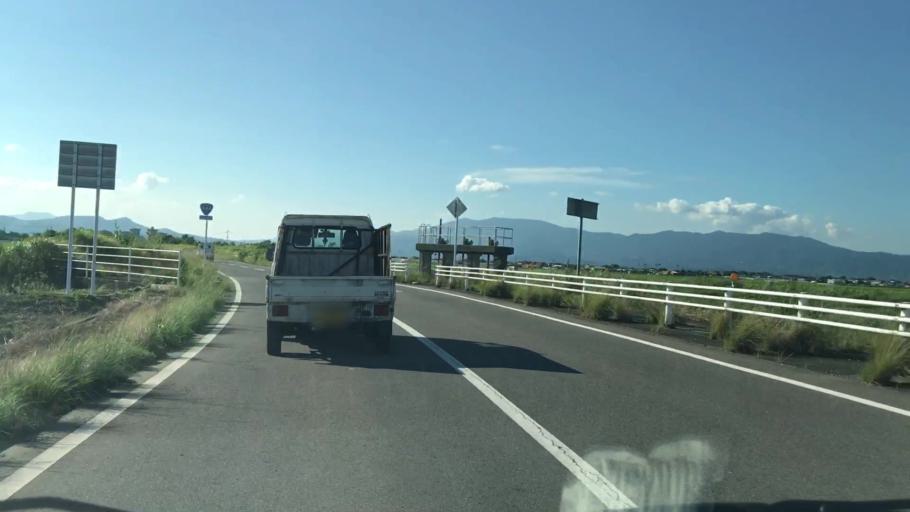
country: JP
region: Saga Prefecture
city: Saga-shi
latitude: 33.2073
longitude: 130.2686
